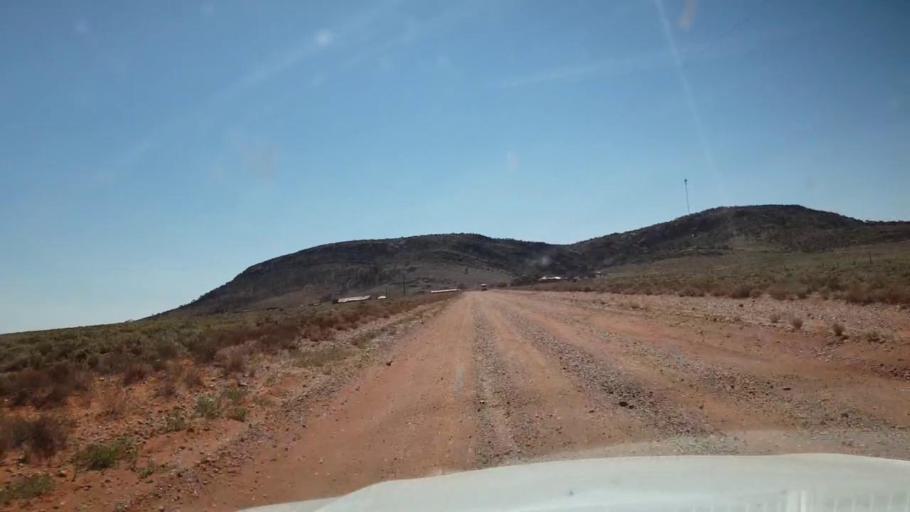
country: AU
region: South Australia
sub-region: Whyalla
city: Whyalla
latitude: -32.6905
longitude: 137.1283
